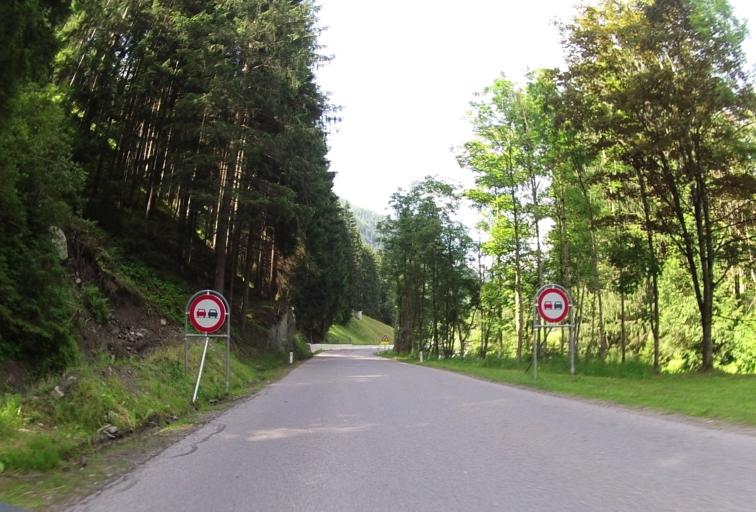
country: AT
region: Tyrol
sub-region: Politischer Bezirk Innsbruck Land
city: Sellrain
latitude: 47.2080
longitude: 11.2006
